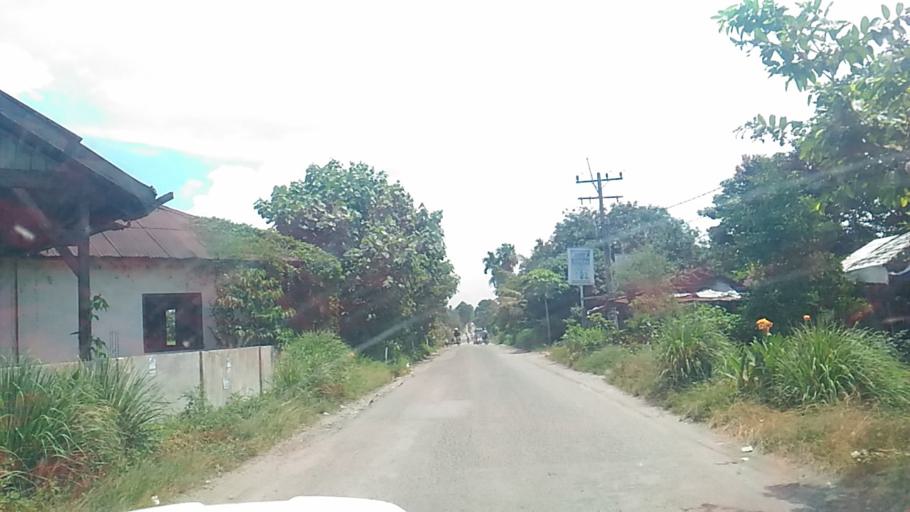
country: ID
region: North Sumatra
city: Sunggal
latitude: 3.5080
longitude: 98.5528
